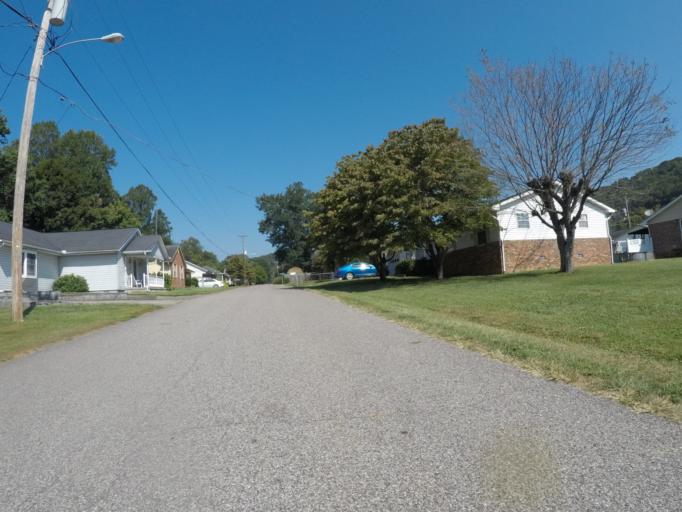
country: US
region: West Virginia
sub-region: Cabell County
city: Barboursville
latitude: 38.3703
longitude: -82.2757
